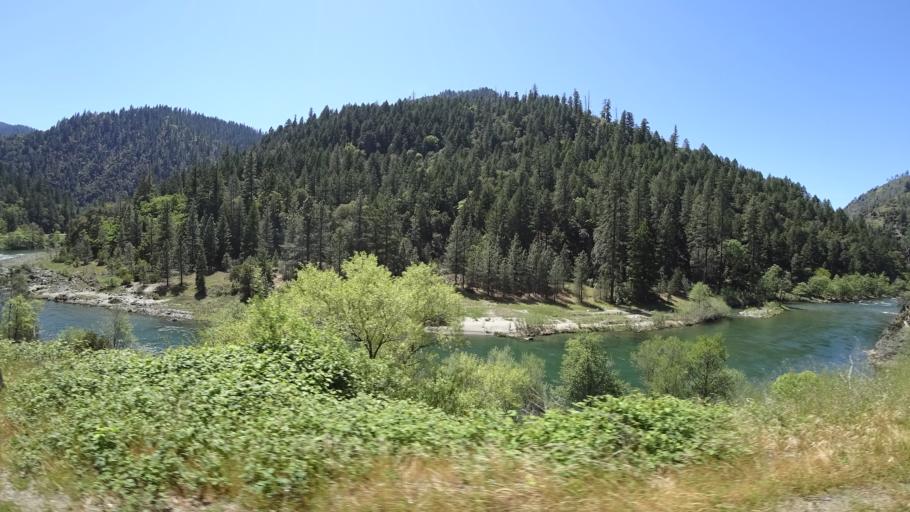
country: US
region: California
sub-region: Trinity County
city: Hayfork
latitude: 40.7905
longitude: -123.3488
